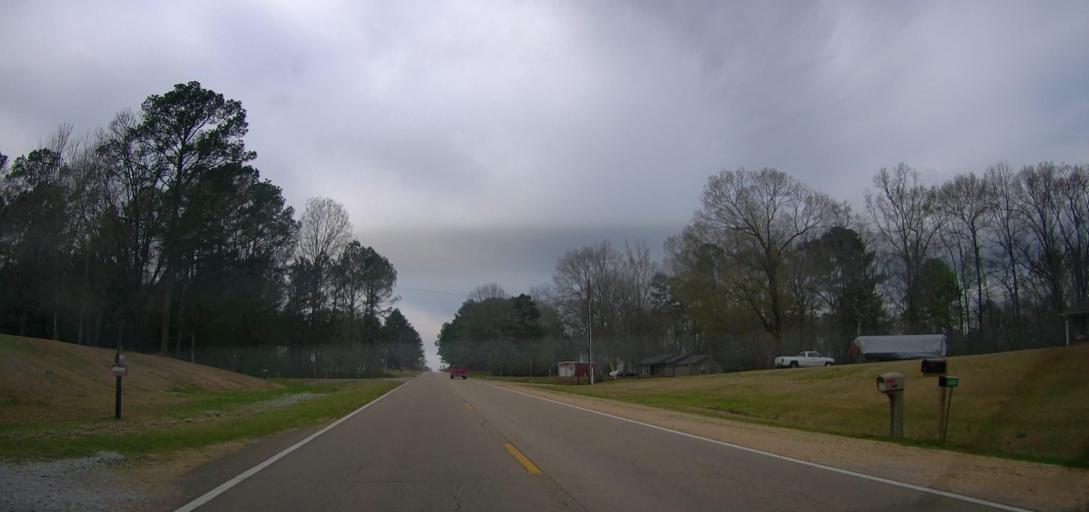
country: US
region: Mississippi
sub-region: Itawamba County
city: Mantachie
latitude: 34.2537
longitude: -88.4827
